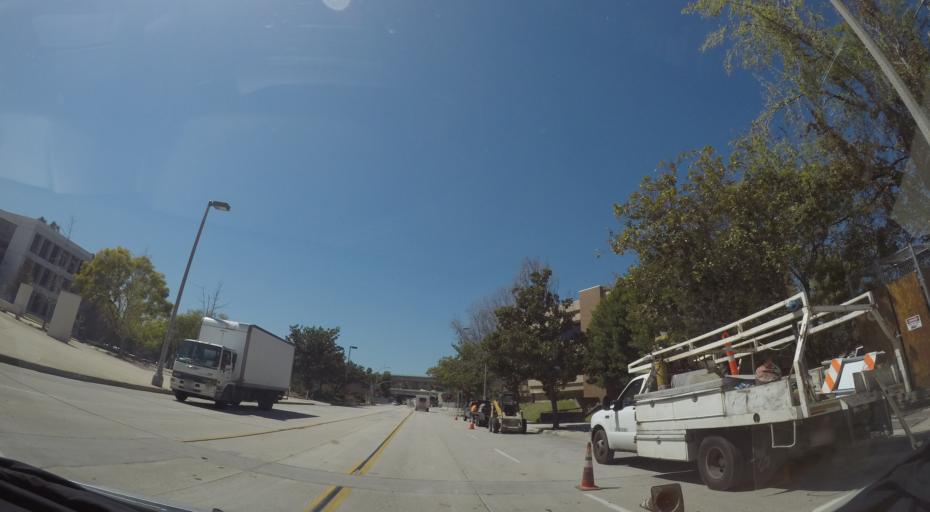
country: US
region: California
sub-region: Los Angeles County
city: Pasadena
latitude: 34.1497
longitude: -118.1522
